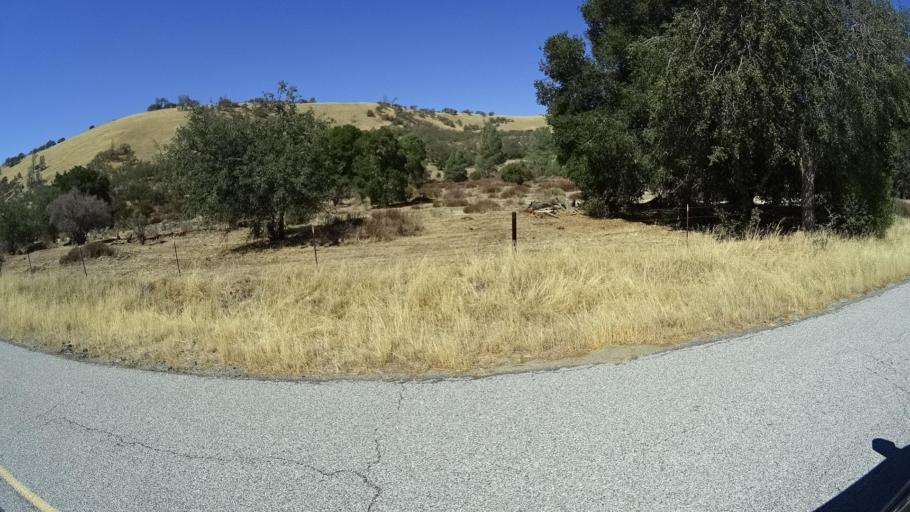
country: US
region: California
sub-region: San Luis Obispo County
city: San Miguel
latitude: 35.8740
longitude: -120.5677
